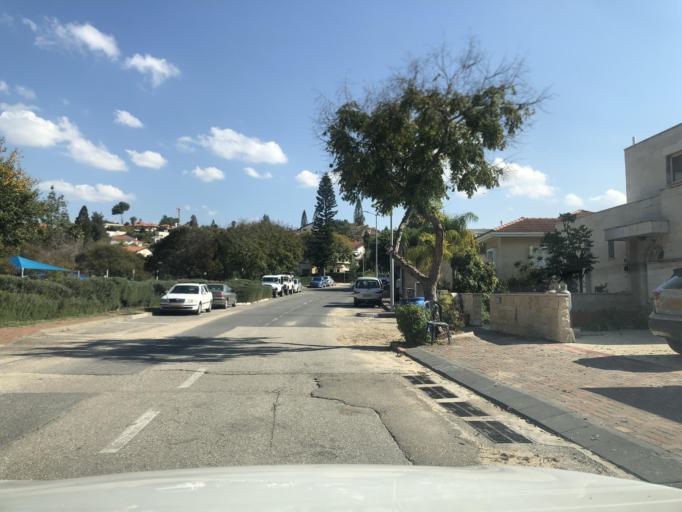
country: PS
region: West Bank
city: Azun Atme
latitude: 32.1122
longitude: 35.0283
